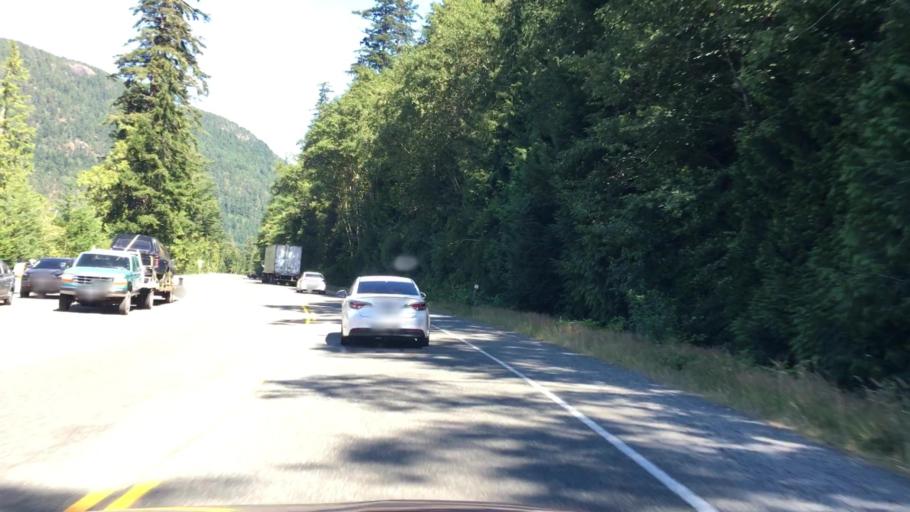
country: CA
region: British Columbia
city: Port Alberni
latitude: 49.2879
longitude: -124.6289
